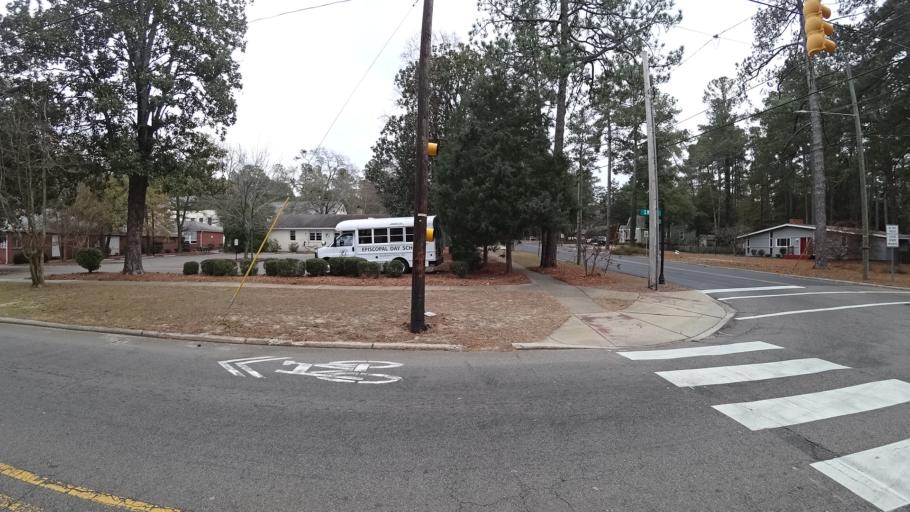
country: US
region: North Carolina
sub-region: Moore County
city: Southern Pines
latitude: 35.1693
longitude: -79.3937
